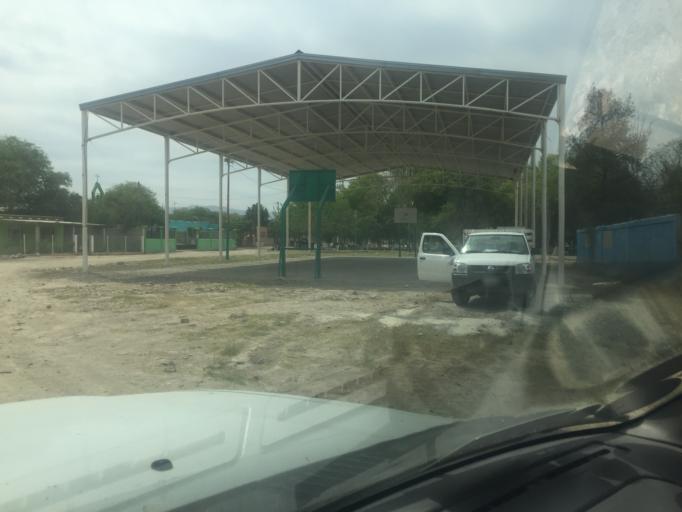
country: MX
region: Durango
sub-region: Gomez Palacio
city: El Vergel
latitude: 25.6721
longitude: -103.5262
